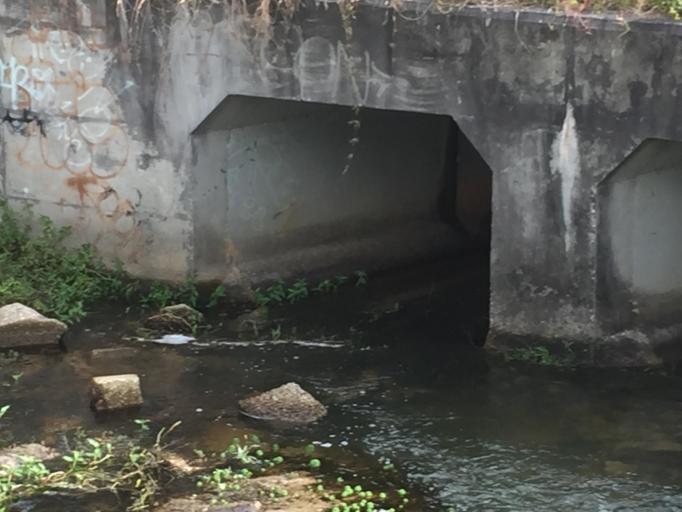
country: US
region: Florida
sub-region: Osceola County
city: Buenaventura Lakes
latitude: 28.3328
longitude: -81.3306
